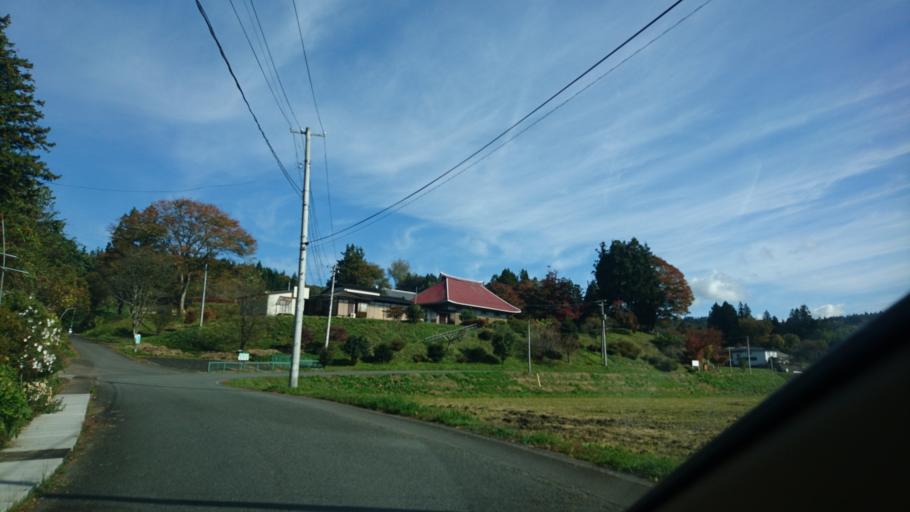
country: JP
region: Iwate
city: Ichinoseki
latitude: 39.0193
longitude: 141.3445
